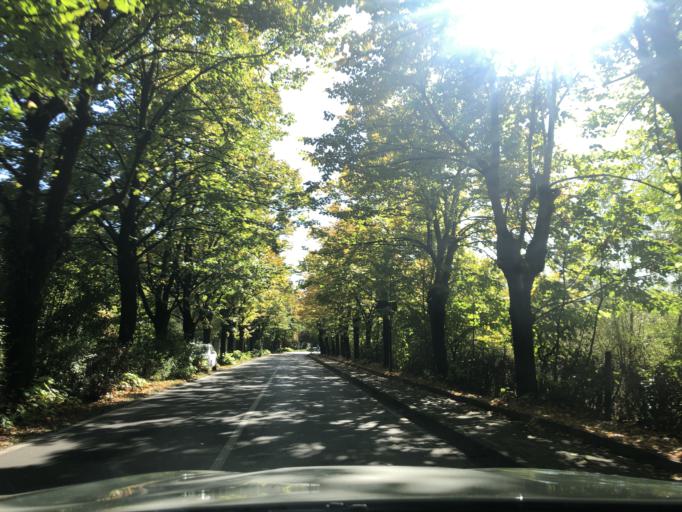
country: IT
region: Lombardy
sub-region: Provincia di Monza e Brianza
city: Villaggio del Sole
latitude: 45.6231
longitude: 9.1193
